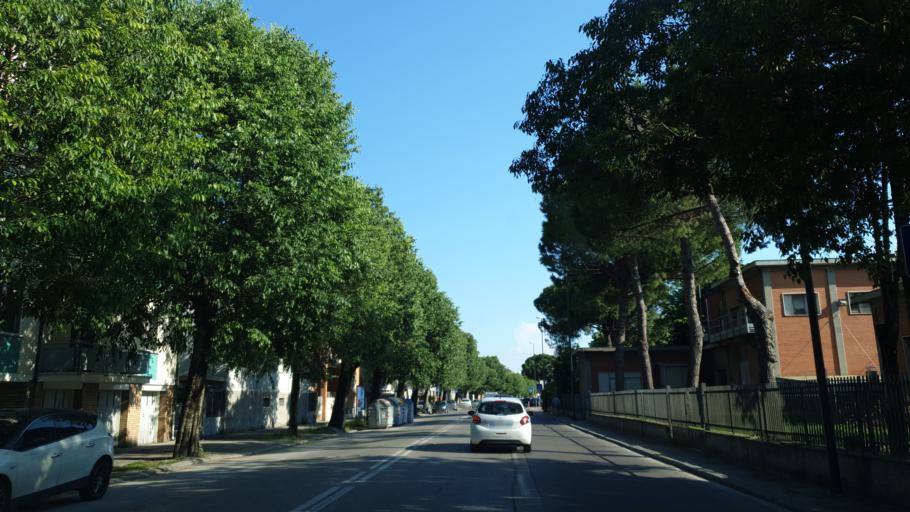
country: IT
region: Emilia-Romagna
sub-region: Provincia di Ravenna
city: Ravenna
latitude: 44.4158
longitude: 12.2105
